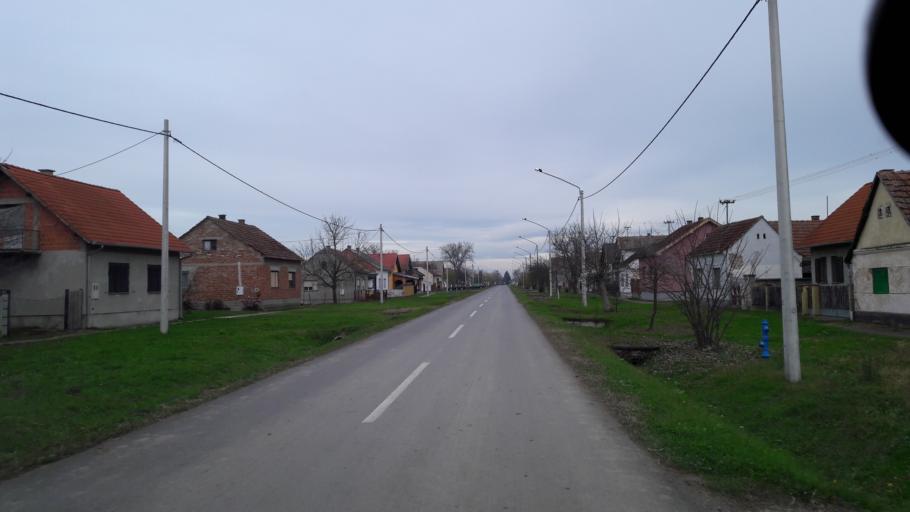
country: HR
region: Osjecko-Baranjska
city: Vladislavci
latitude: 45.4471
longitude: 18.5611
